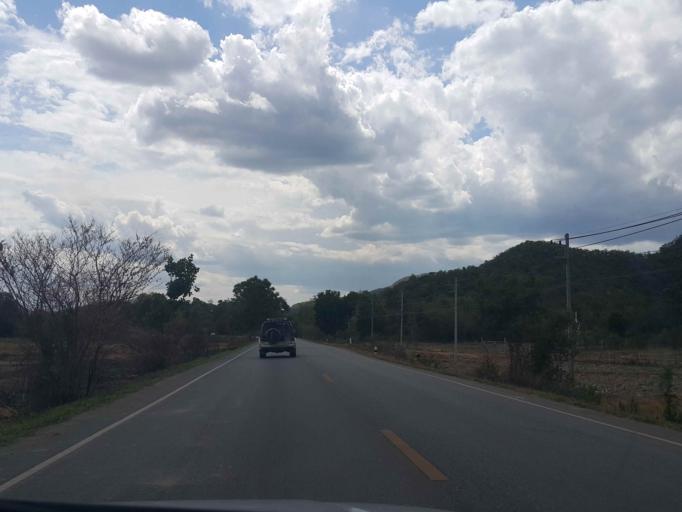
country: TH
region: Sukhothai
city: Thung Saliam
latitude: 17.3332
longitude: 99.4958
